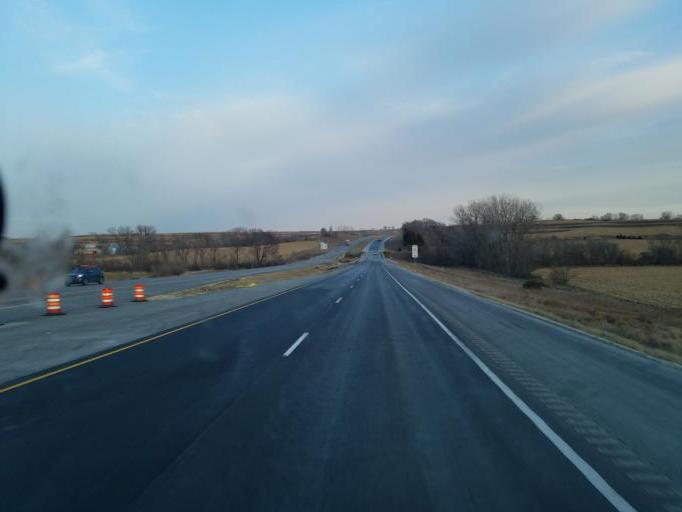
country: US
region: Iowa
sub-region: Harrison County
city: Logan
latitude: 41.4989
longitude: -95.7338
